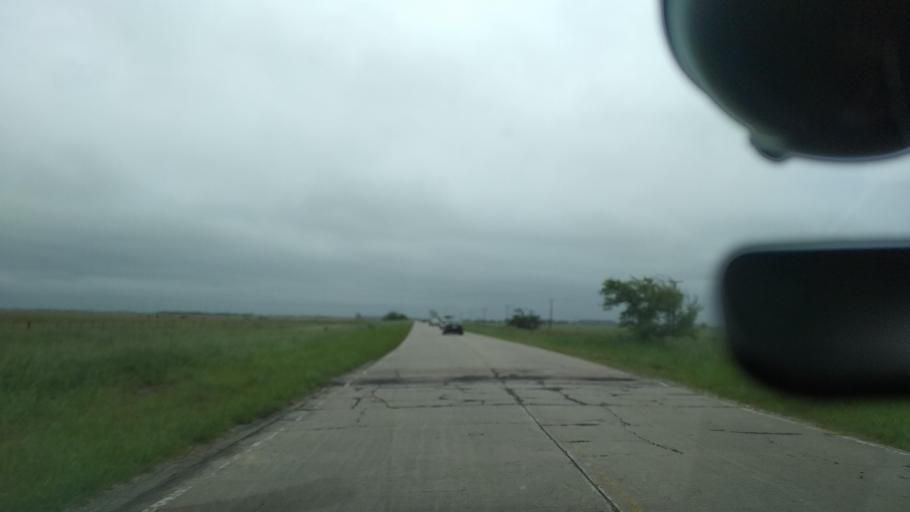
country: AR
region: Buenos Aires
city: Veronica
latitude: -35.5646
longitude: -57.2939
